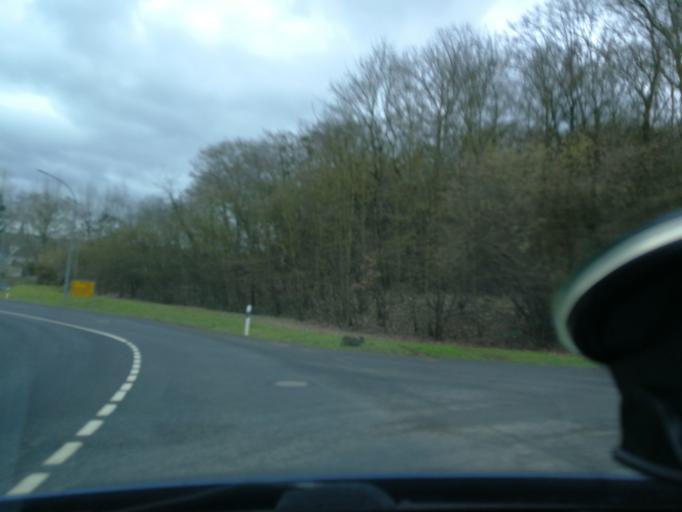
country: DE
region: Rheinland-Pfalz
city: Oberbillig
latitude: 49.7234
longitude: 6.4936
